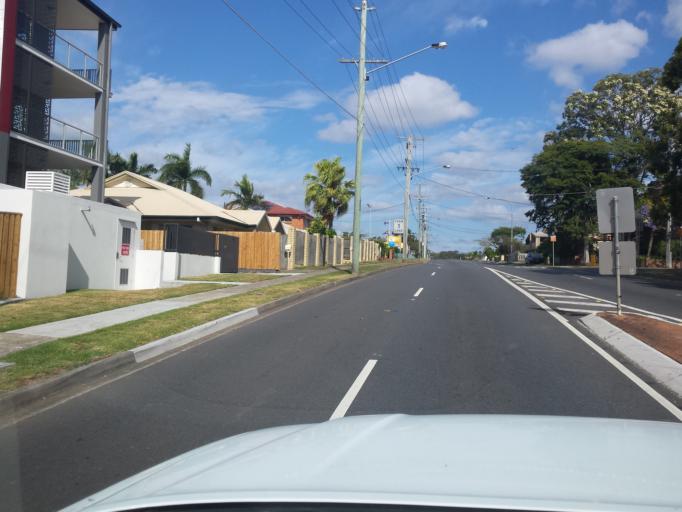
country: AU
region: Queensland
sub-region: Brisbane
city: Wavell Heights
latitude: -27.3933
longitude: 153.0302
